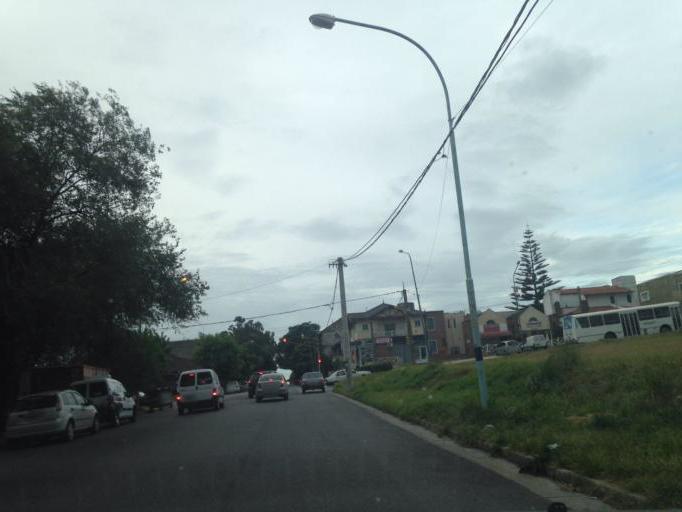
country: AR
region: Buenos Aires
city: Mar del Plata
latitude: -38.0229
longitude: -57.5574
